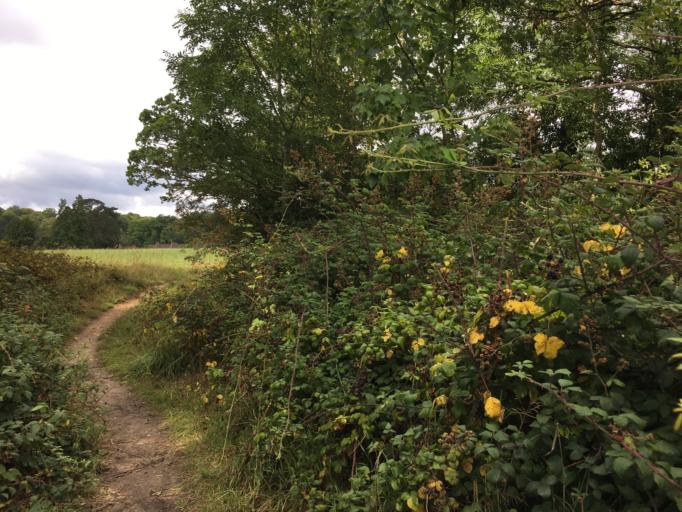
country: GB
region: England
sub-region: Hampshire
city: Lyndhurst
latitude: 50.8726
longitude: -1.5834
